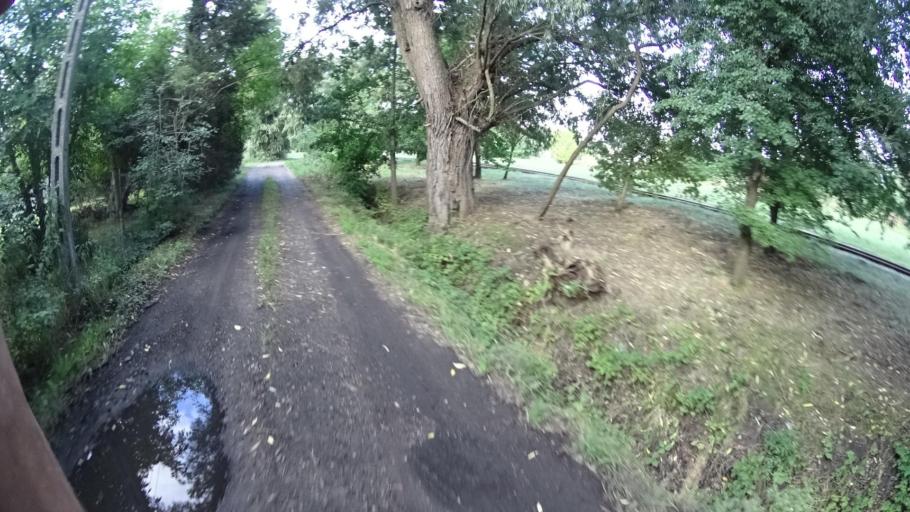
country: PL
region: Masovian Voivodeship
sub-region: Powiat piaseczynski
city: Tarczyn
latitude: 51.9800
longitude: 20.8719
